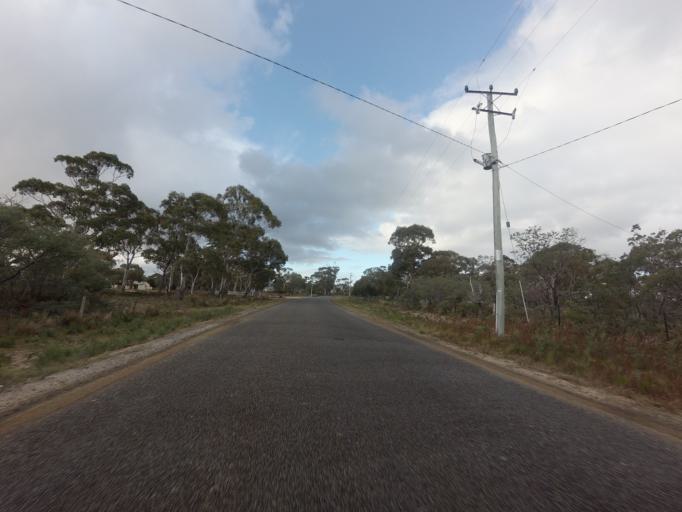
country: AU
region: Tasmania
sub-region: Break O'Day
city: St Helens
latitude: -42.1022
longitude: 148.0805
